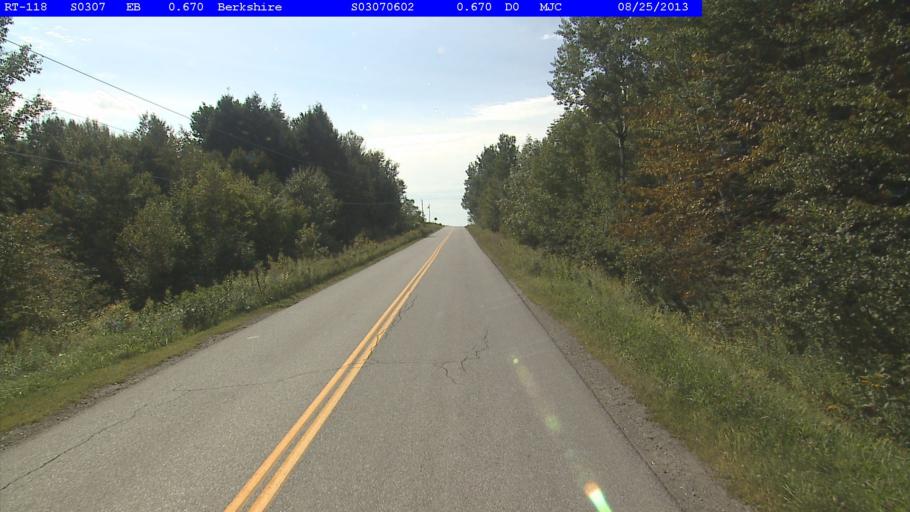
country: US
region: Vermont
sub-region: Franklin County
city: Richford
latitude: 44.9356
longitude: -72.7247
